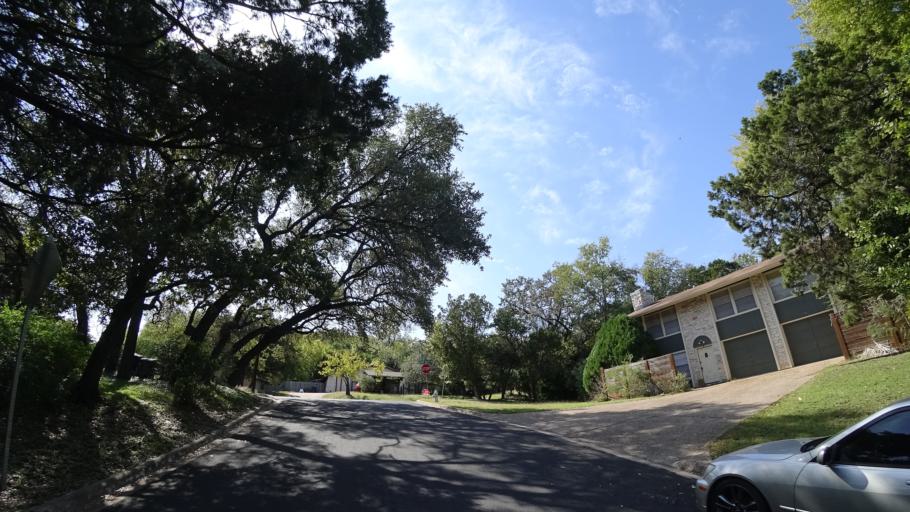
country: US
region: Texas
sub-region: Travis County
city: West Lake Hills
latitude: 30.3505
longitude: -97.7591
